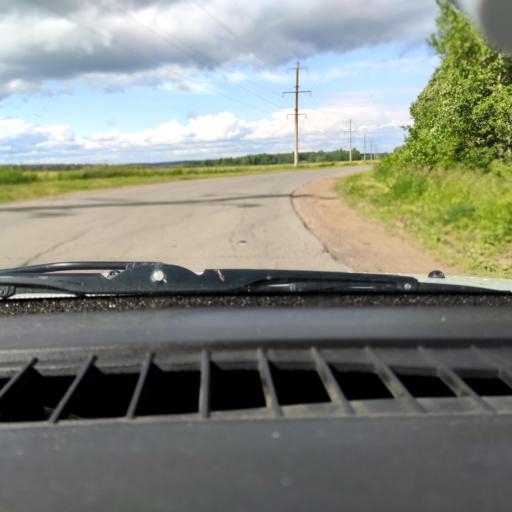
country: RU
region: Perm
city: Uinskoye
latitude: 57.1272
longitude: 56.5568
